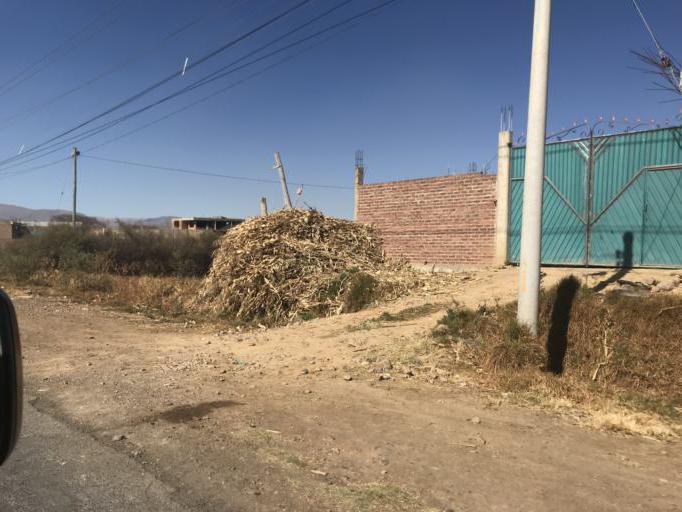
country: BO
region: Cochabamba
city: Cliza
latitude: -17.5722
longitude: -65.8989
